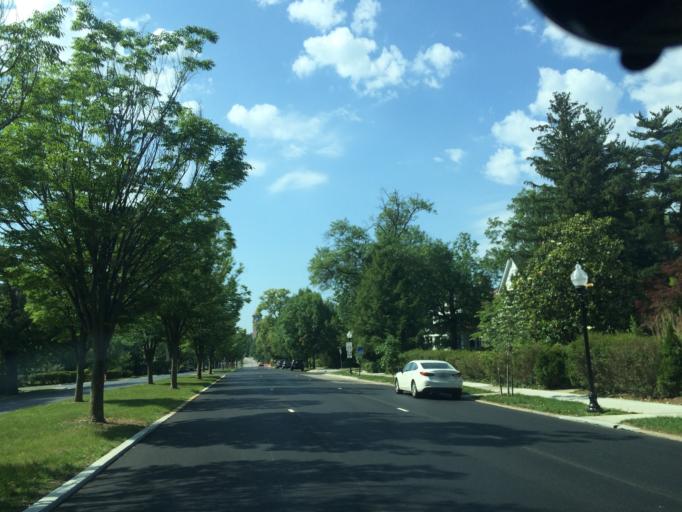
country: US
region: Maryland
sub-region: City of Baltimore
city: Baltimore
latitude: 39.3466
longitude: -76.6359
